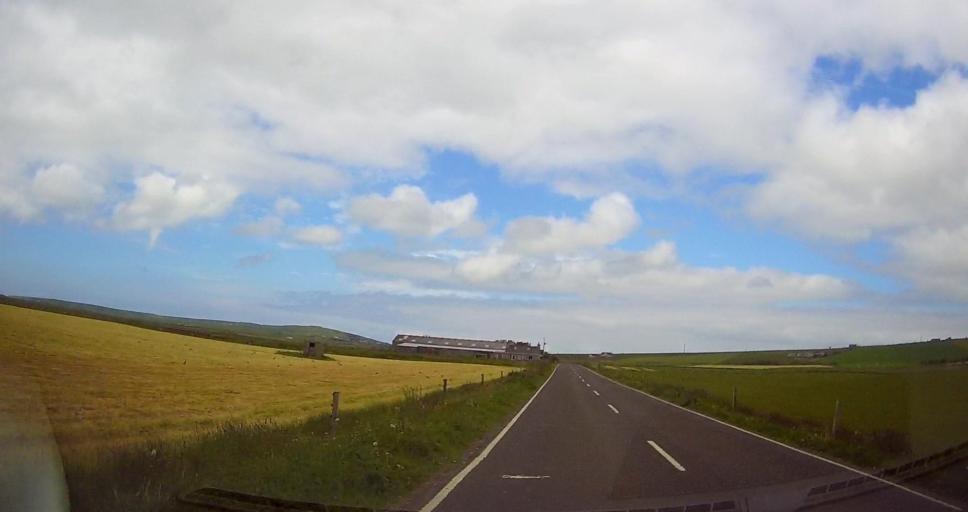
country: GB
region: Scotland
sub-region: Orkney Islands
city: Stromness
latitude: 59.0831
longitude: -3.2546
